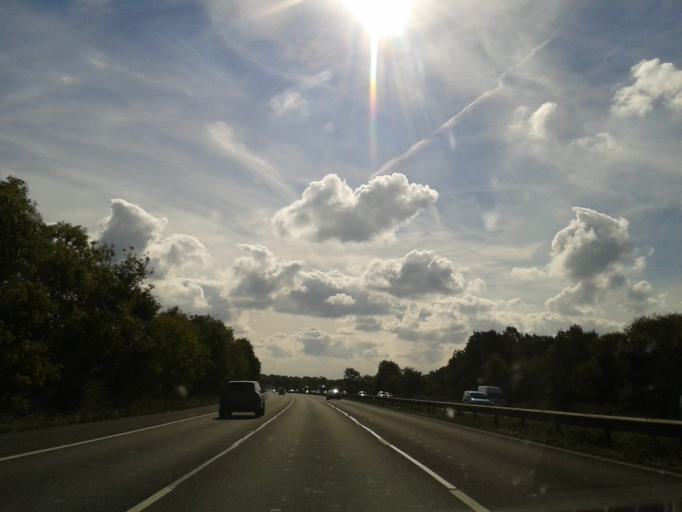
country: GB
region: England
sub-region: Staffordshire
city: Stone
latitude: 52.9037
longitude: -2.1902
